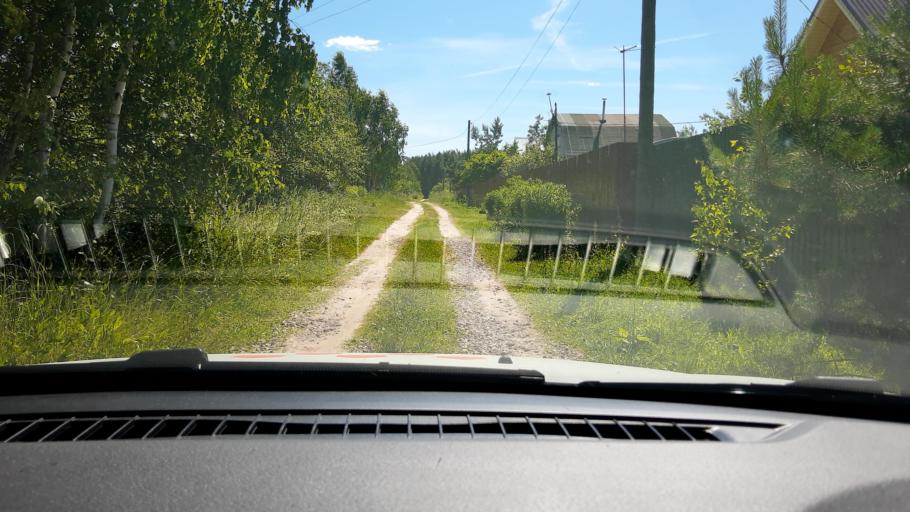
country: RU
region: Nizjnij Novgorod
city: Surovatikha
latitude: 55.8691
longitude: 43.9647
